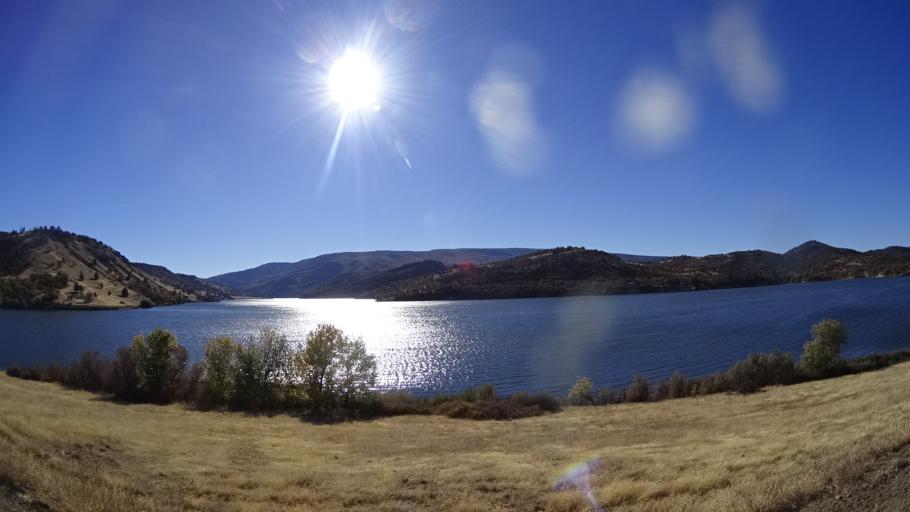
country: US
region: California
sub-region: Siskiyou County
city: Montague
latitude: 41.9897
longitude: -122.3180
